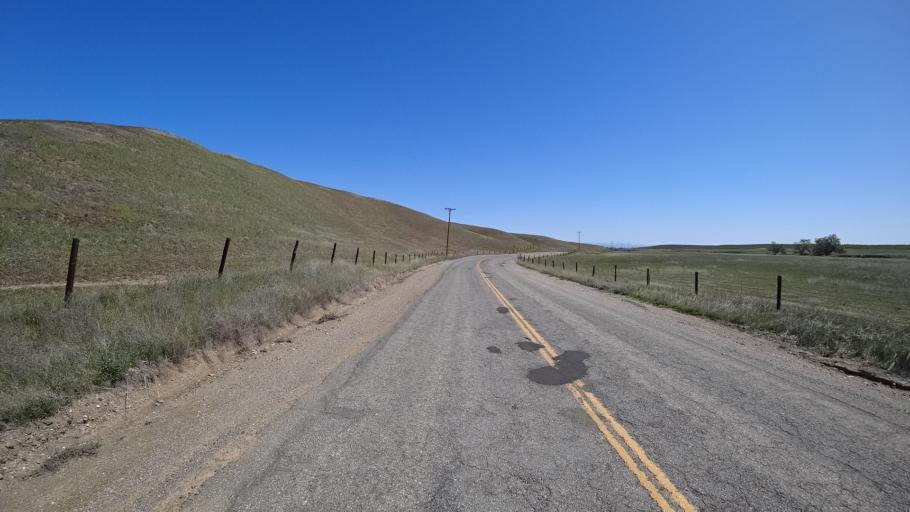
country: US
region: California
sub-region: Glenn County
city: Orland
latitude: 39.7801
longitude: -122.3072
